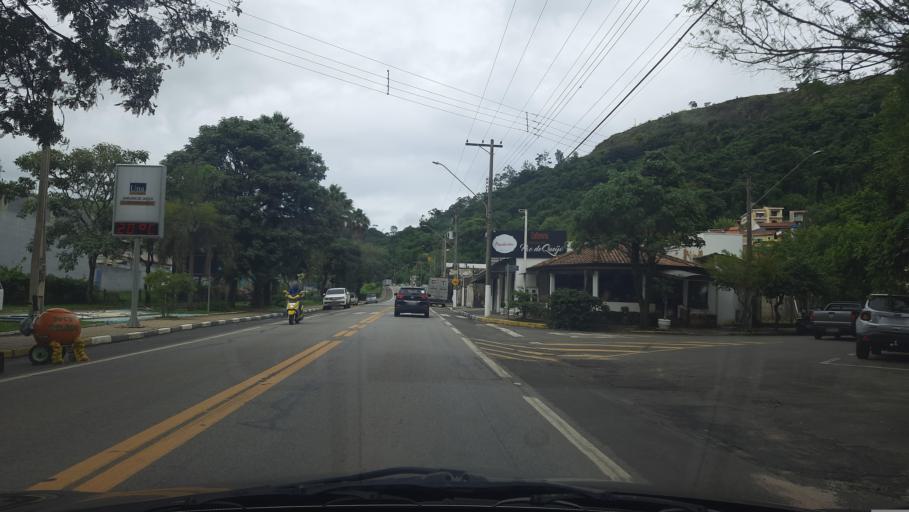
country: BR
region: Sao Paulo
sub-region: Sao Joao Da Boa Vista
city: Sao Joao da Boa Vista
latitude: -21.9419
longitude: -46.7160
